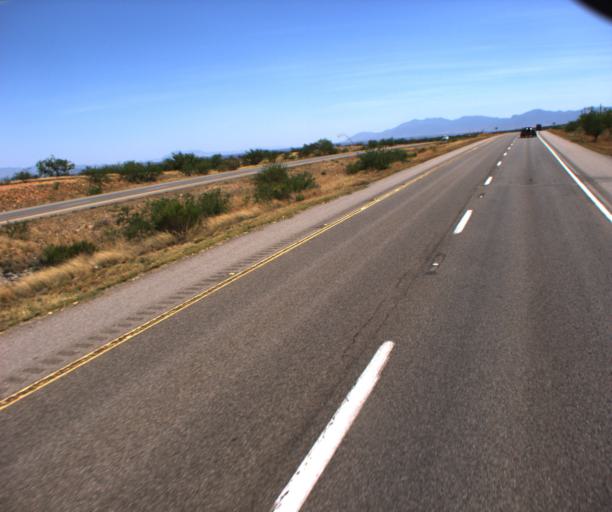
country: US
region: Arizona
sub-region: Cochise County
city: Whetstone
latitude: 31.8483
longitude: -110.3415
